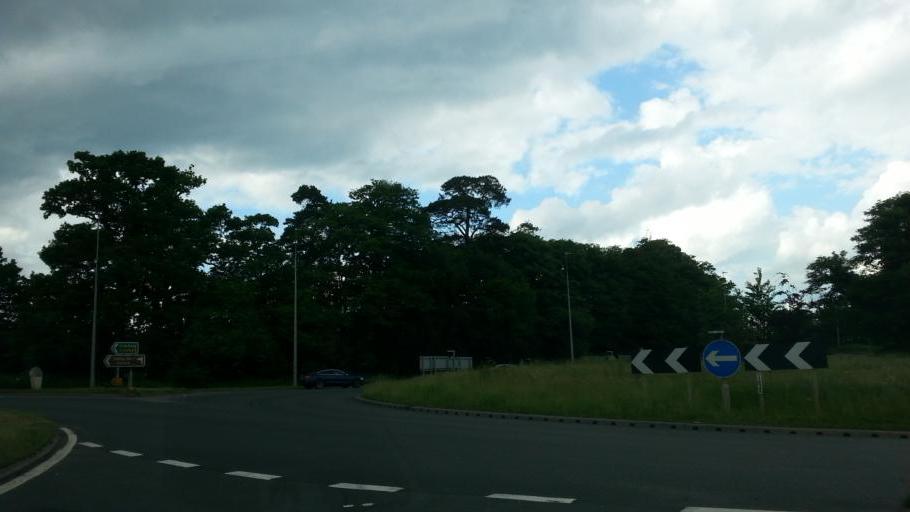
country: GB
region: England
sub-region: Warwickshire
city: Curdworth
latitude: 52.5507
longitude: -1.7318
